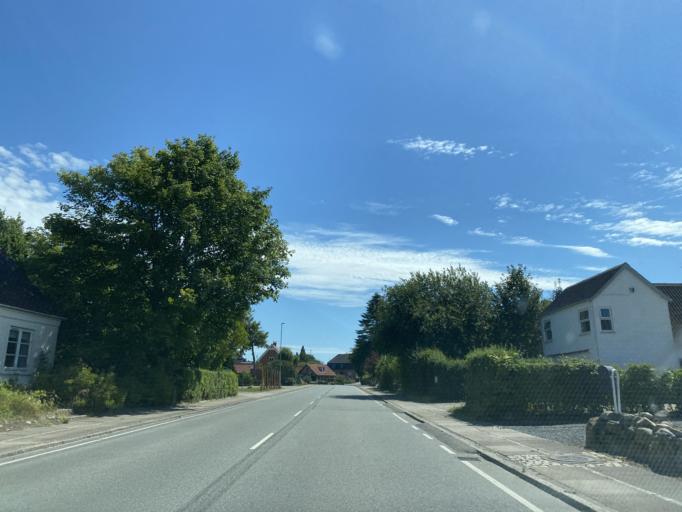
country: DK
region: South Denmark
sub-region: Faaborg-Midtfyn Kommune
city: Ringe
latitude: 55.2370
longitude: 10.5618
